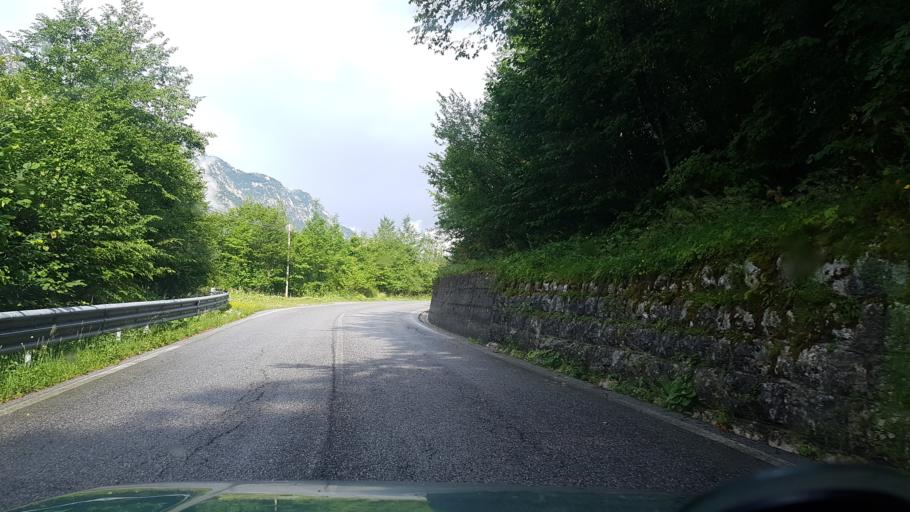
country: IT
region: Friuli Venezia Giulia
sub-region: Provincia di Udine
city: Lusevera
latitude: 46.3054
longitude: 13.2880
